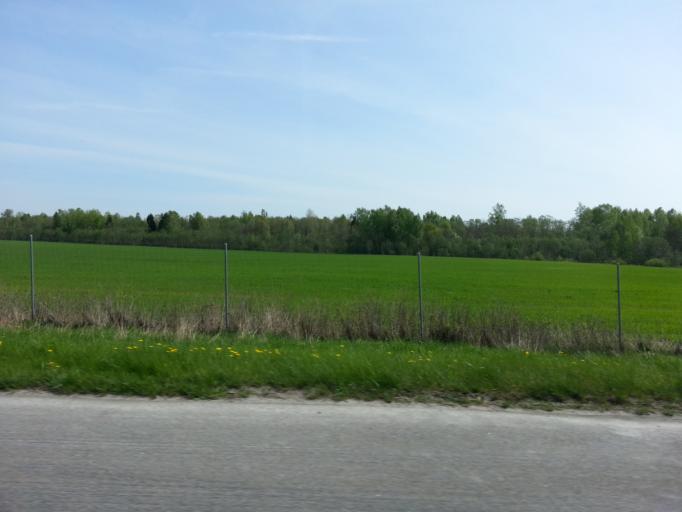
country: LT
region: Vilnius County
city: Ukmerge
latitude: 55.4813
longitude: 24.6400
